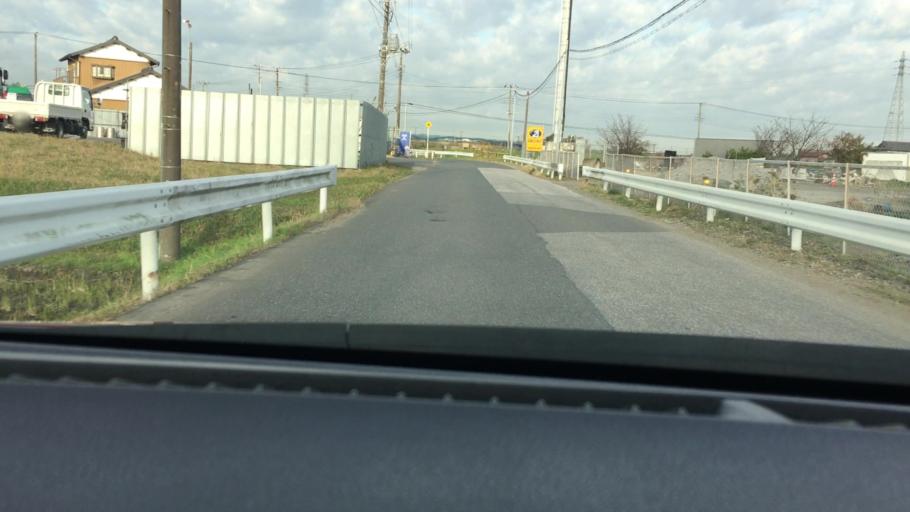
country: JP
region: Chiba
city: Kisarazu
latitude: 35.4074
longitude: 139.9580
